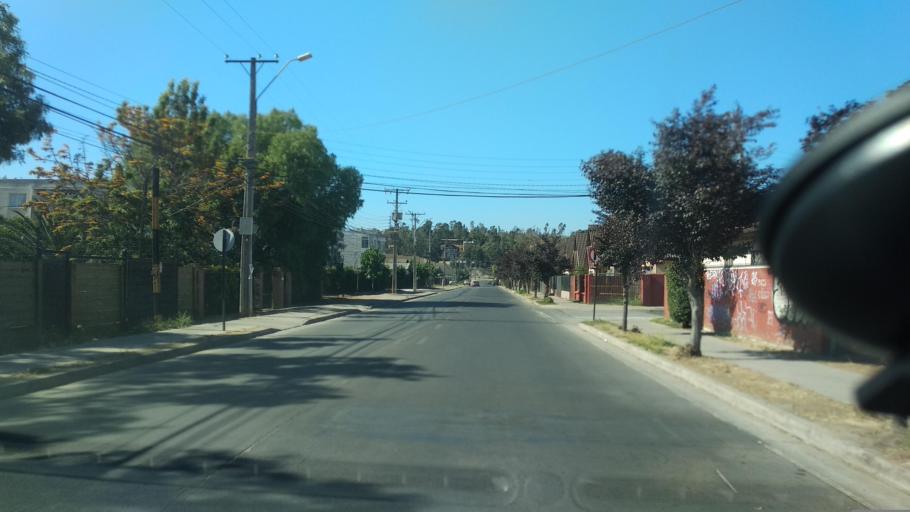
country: CL
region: Valparaiso
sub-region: Provincia de Marga Marga
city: Villa Alemana
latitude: -33.0423
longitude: -71.3904
